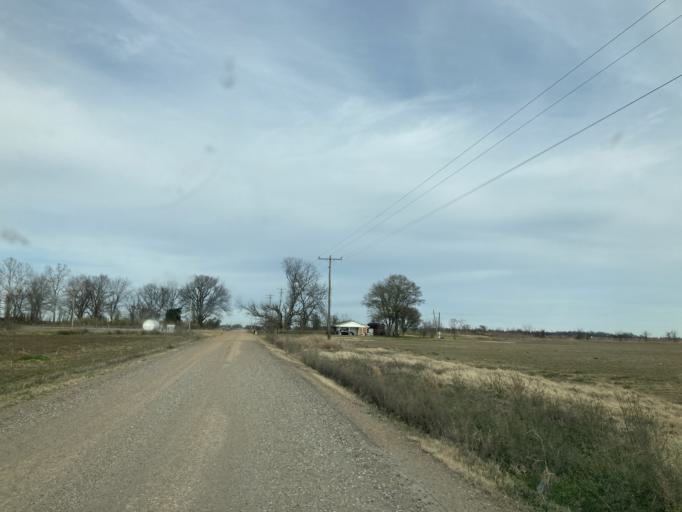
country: US
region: Mississippi
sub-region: Humphreys County
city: Belzoni
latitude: 33.1511
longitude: -90.6067
